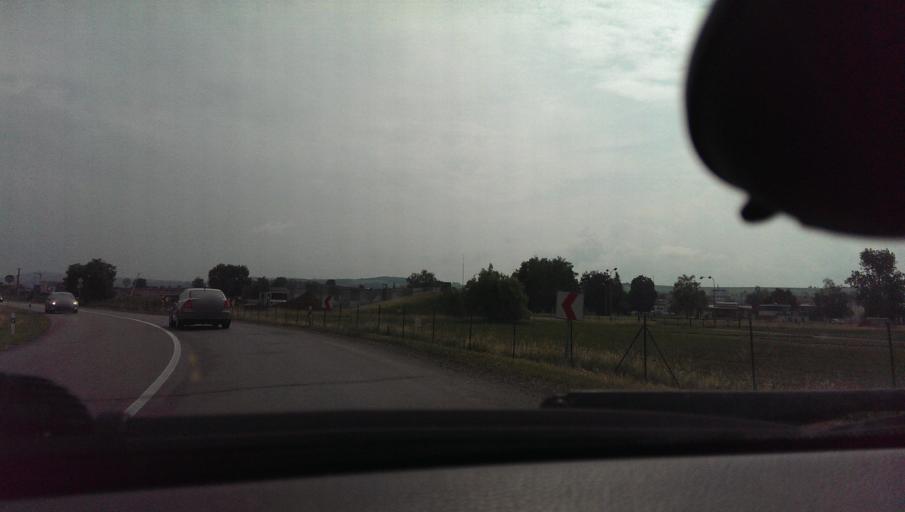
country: CZ
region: Zlin
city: Otrokovice
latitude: 49.1979
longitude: 17.5206
